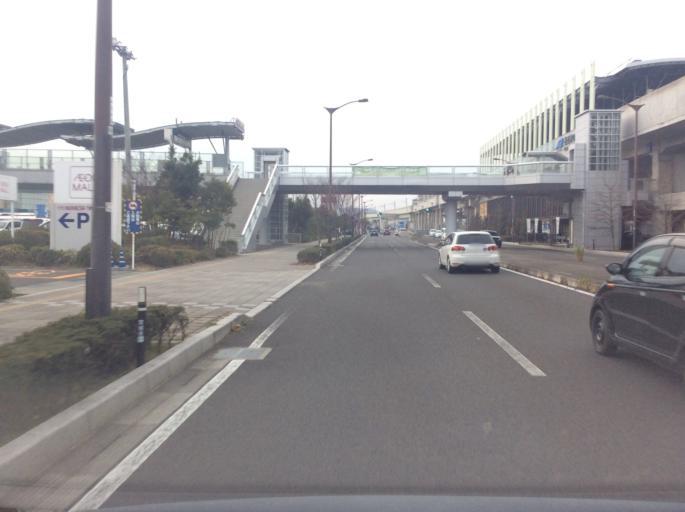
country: JP
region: Miyagi
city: Iwanuma
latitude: 38.1650
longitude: 140.8971
